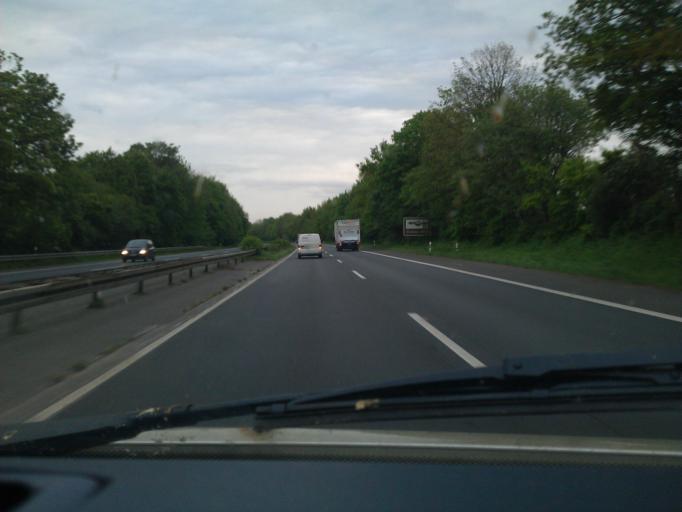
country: DE
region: North Rhine-Westphalia
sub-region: Regierungsbezirk Koln
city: Aldenhoven
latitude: 50.9022
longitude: 6.2918
